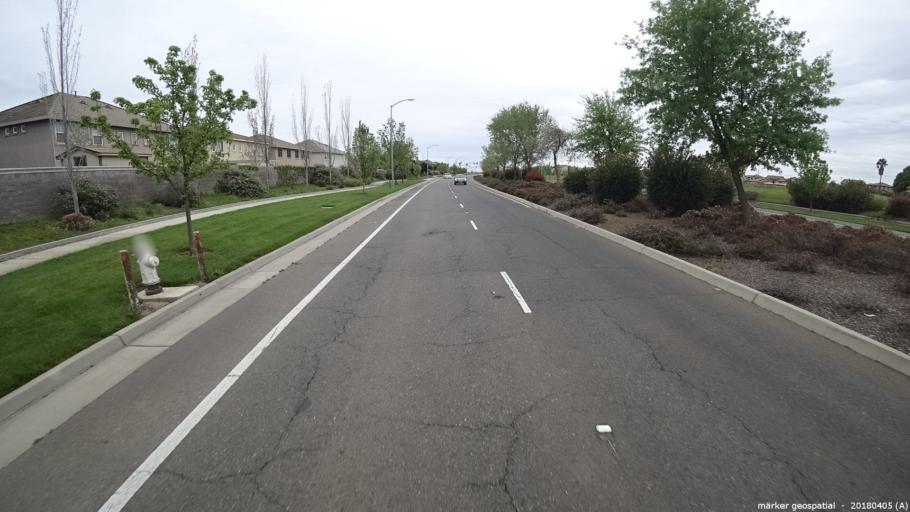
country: US
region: California
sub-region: Sacramento County
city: Laguna
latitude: 38.3815
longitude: -121.4484
